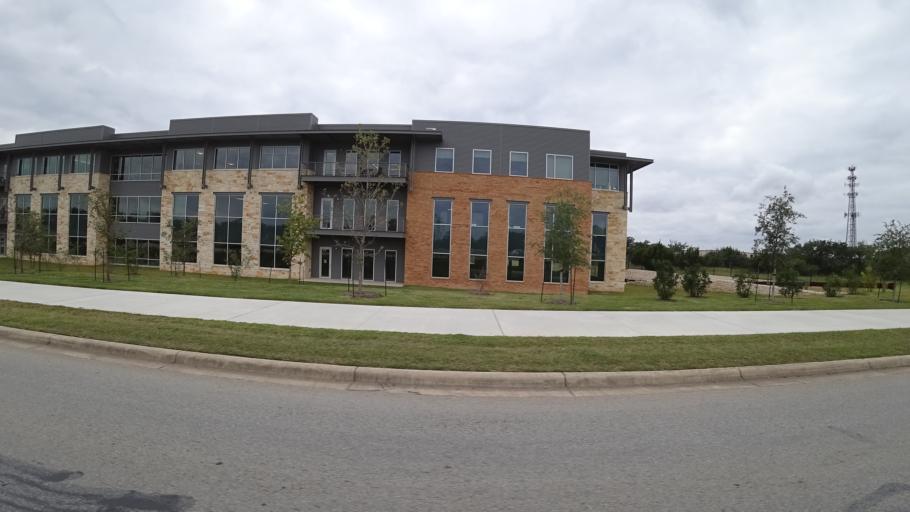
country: US
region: Texas
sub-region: Travis County
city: Bee Cave
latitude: 30.3146
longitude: -97.9456
